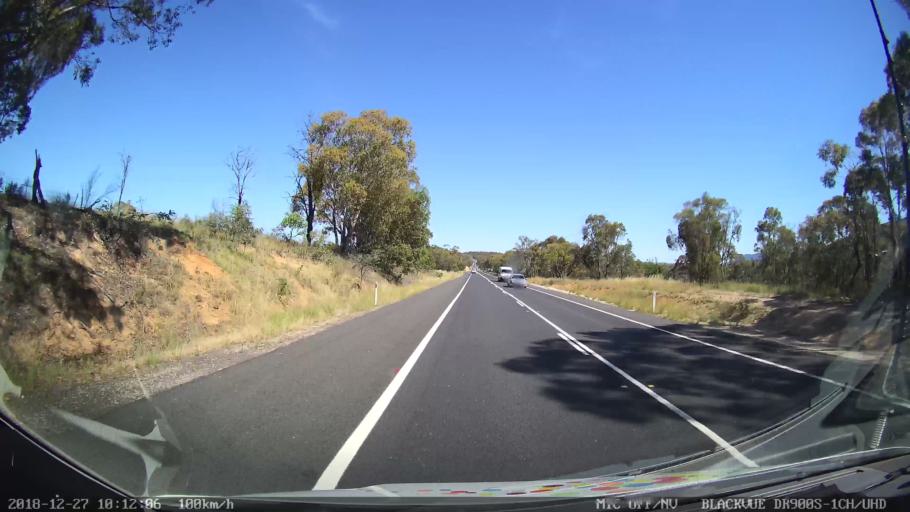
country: AU
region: New South Wales
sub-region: Bathurst Regional
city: Kelso
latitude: -33.4469
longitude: 149.7645
